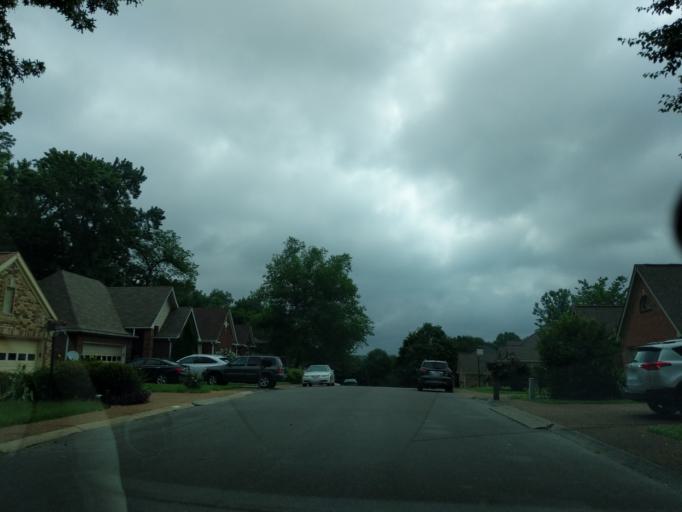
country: US
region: Tennessee
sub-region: Davidson County
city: Lakewood
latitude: 36.1741
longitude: -86.6183
